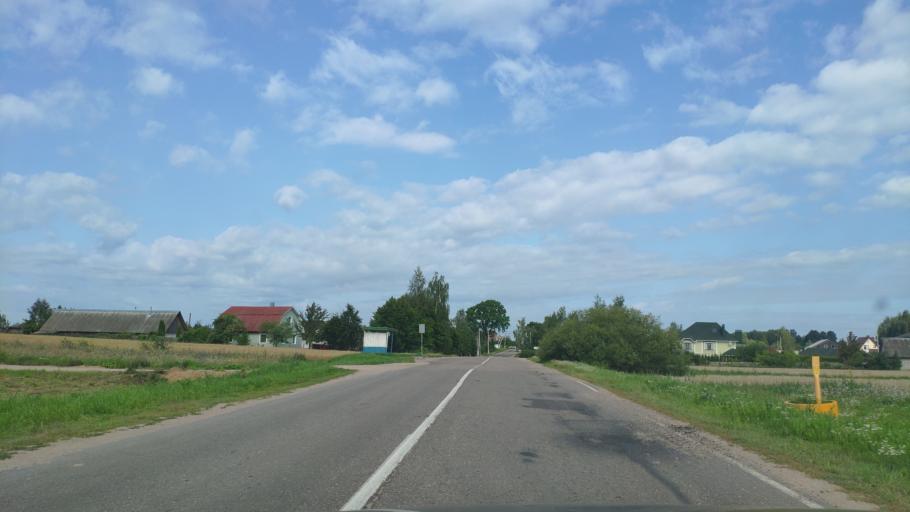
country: BY
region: Minsk
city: Khatsyezhyna
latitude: 53.8812
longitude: 27.2783
